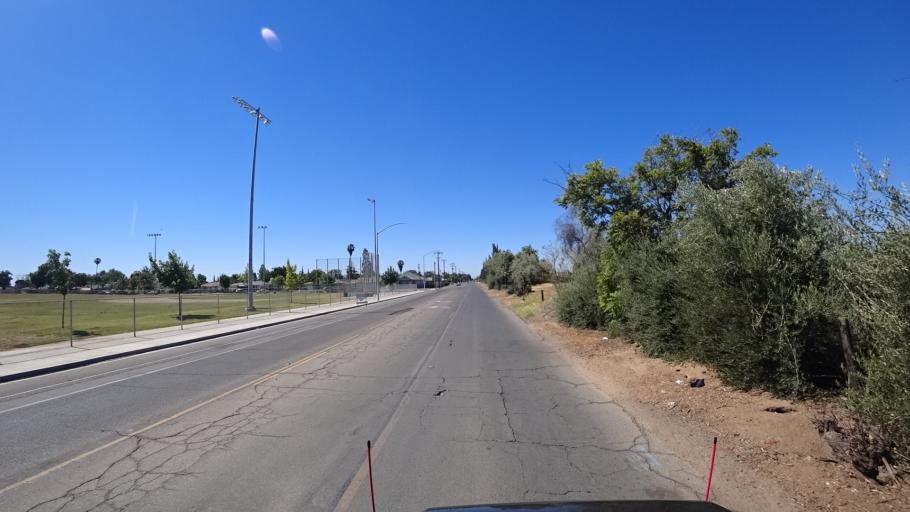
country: US
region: California
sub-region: Fresno County
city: Fresno
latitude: 36.7114
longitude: -119.7999
